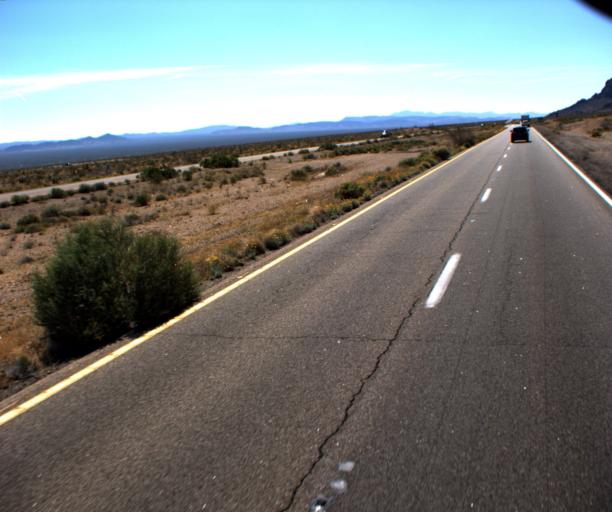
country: US
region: Nevada
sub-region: Clark County
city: Boulder City
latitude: 35.8226
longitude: -114.5551
